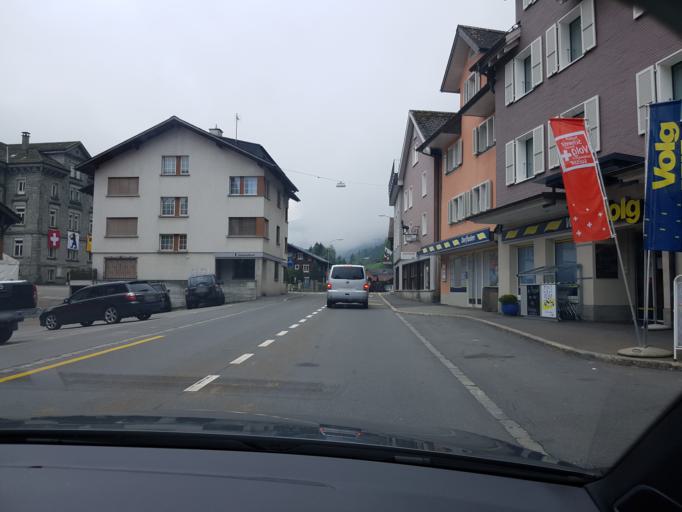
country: CH
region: Uri
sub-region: Uri
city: Andermatt
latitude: 46.7065
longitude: 8.5995
